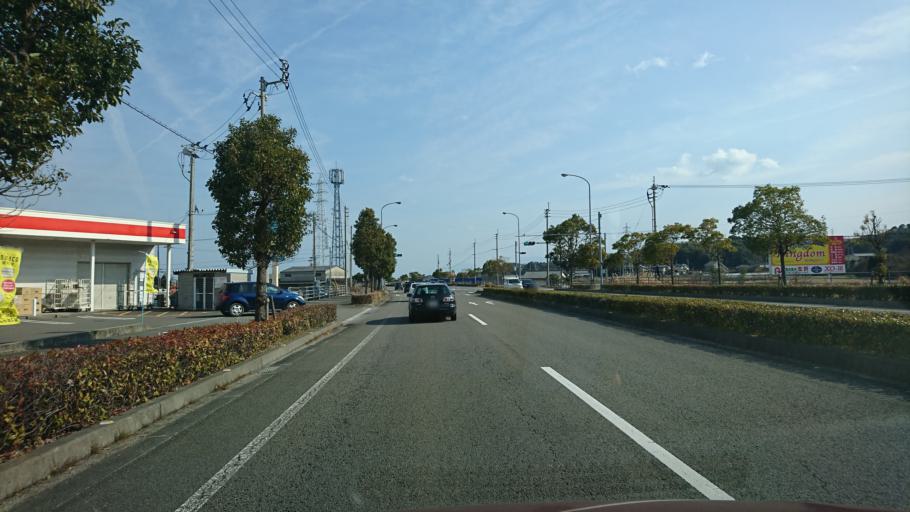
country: JP
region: Ehime
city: Saijo
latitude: 34.0197
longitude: 133.0169
